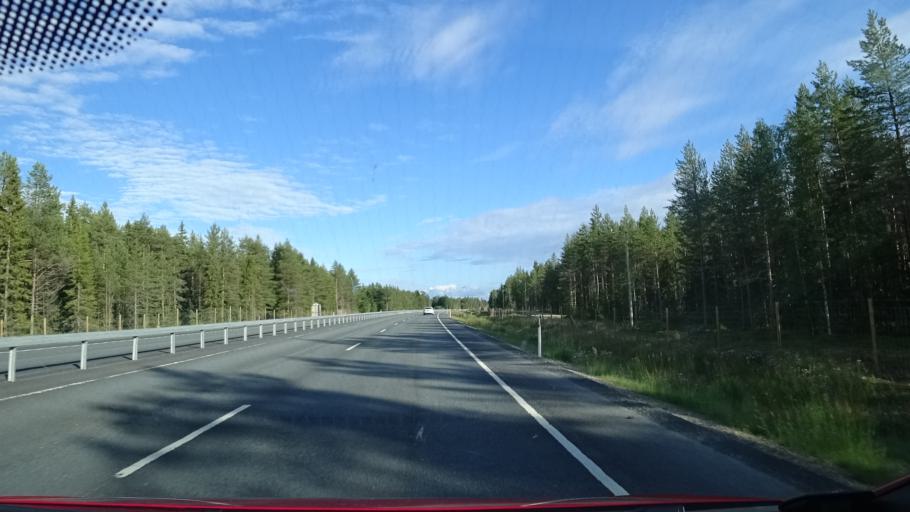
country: FI
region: Northern Ostrobothnia
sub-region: Oulunkaari
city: Kuivaniemi
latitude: 65.5172
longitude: 25.2779
